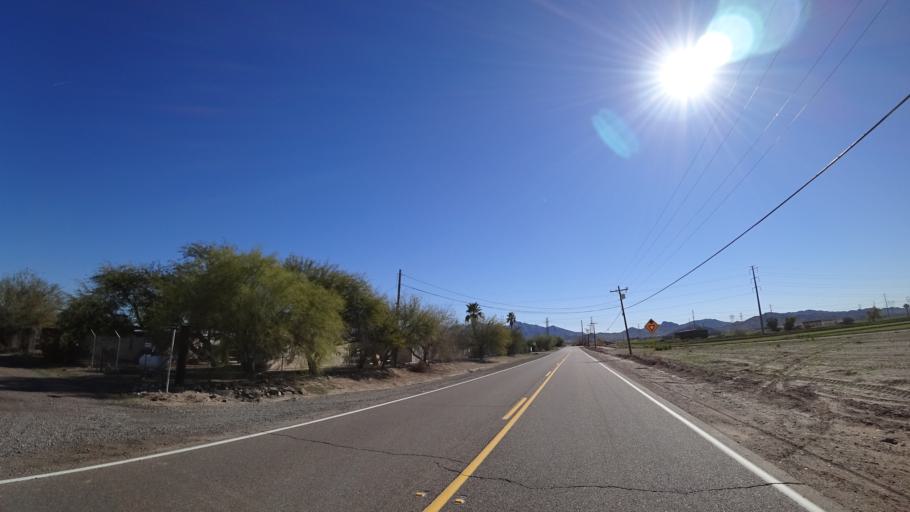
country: US
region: Arizona
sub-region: Maricopa County
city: Goodyear
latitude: 33.4091
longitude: -112.3575
